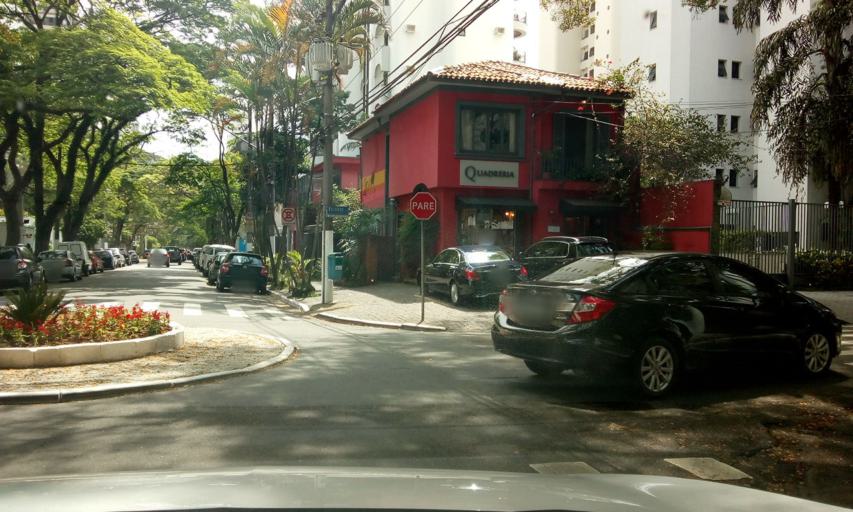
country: BR
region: Sao Paulo
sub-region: Sao Paulo
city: Sao Paulo
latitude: -23.5946
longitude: -46.6670
